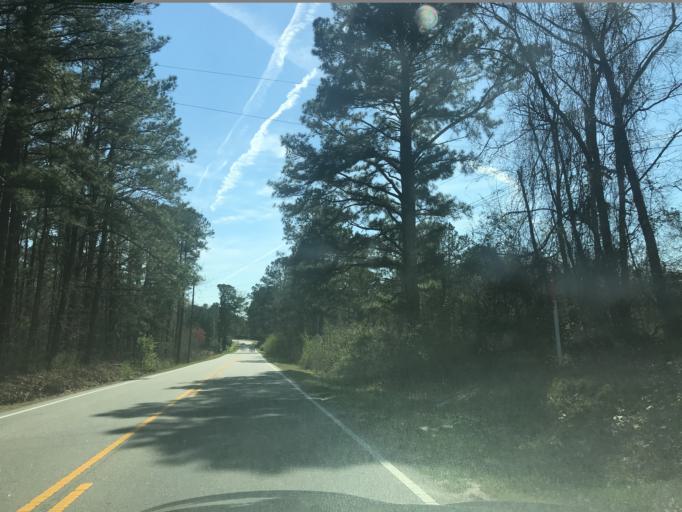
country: US
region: North Carolina
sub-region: Wake County
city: Fuquay-Varina
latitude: 35.5704
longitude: -78.7717
